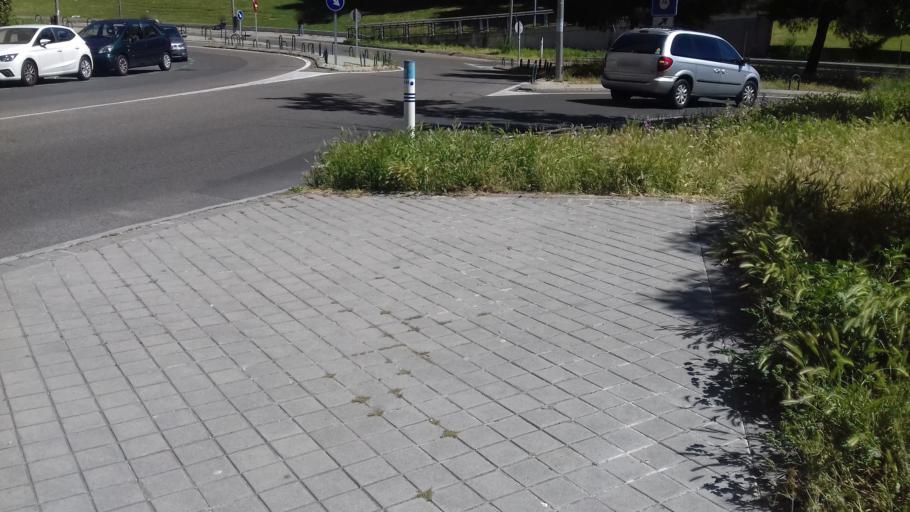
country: ES
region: Madrid
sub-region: Provincia de Madrid
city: Moratalaz
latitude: 40.4135
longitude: -3.6624
